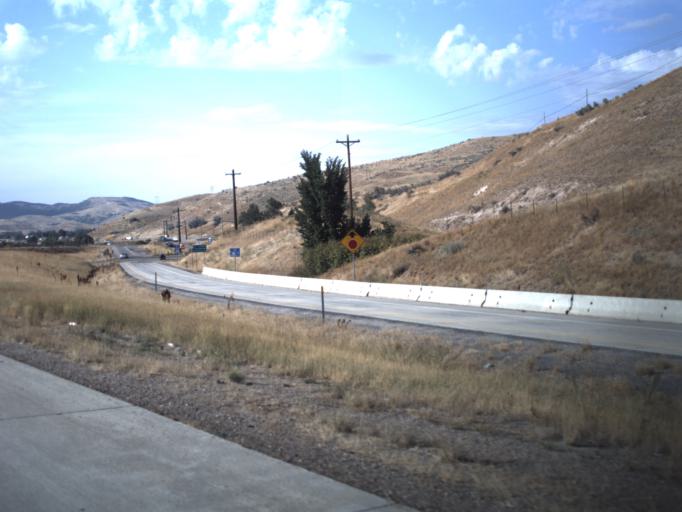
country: US
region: Utah
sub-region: Morgan County
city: Mountain Green
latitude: 41.1138
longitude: -111.7622
